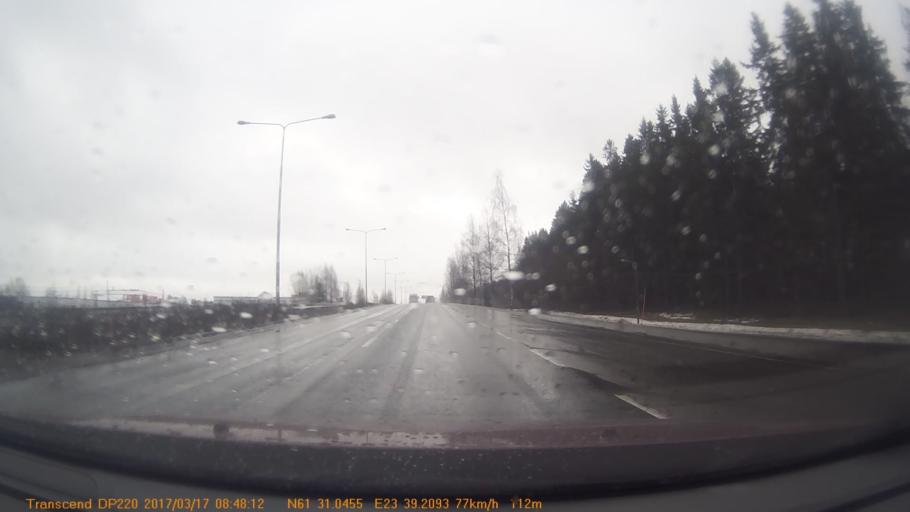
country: FI
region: Pirkanmaa
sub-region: Tampere
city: Pirkkala
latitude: 61.5173
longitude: 23.6538
